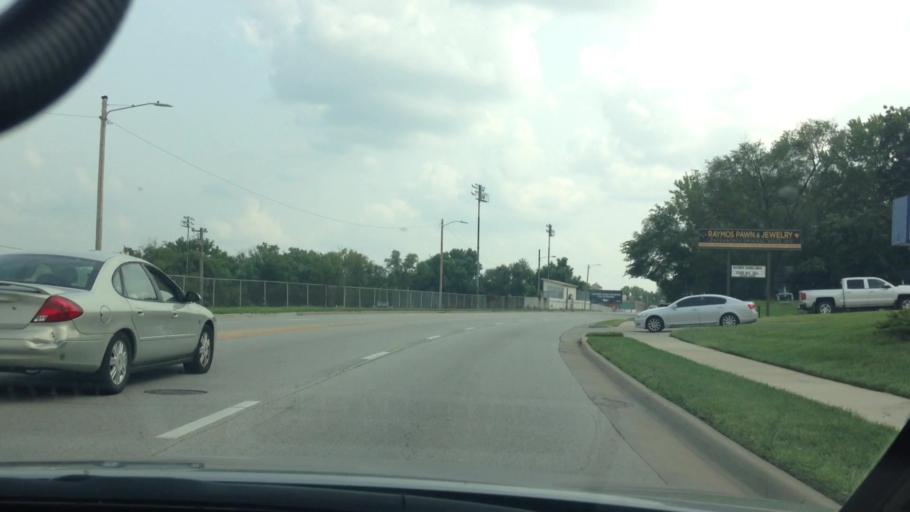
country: US
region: Kansas
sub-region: Leavenworth County
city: Leavenworth
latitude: 39.3030
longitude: -94.9091
